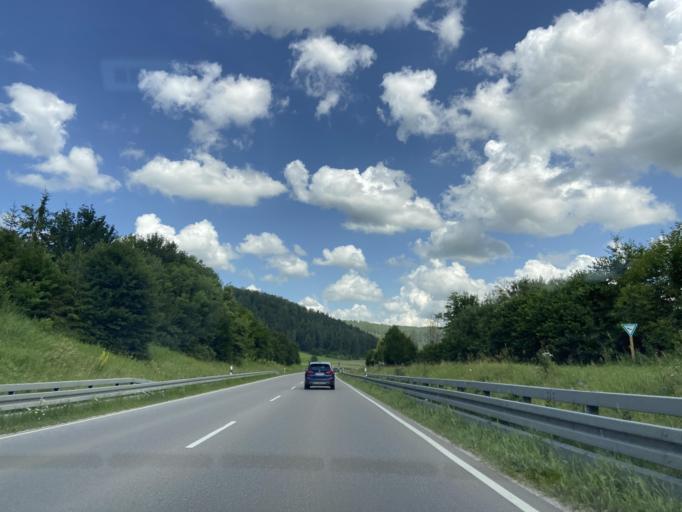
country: DE
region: Baden-Wuerttemberg
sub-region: Tuebingen Region
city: Strassberg
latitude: 48.1922
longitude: 9.0703
